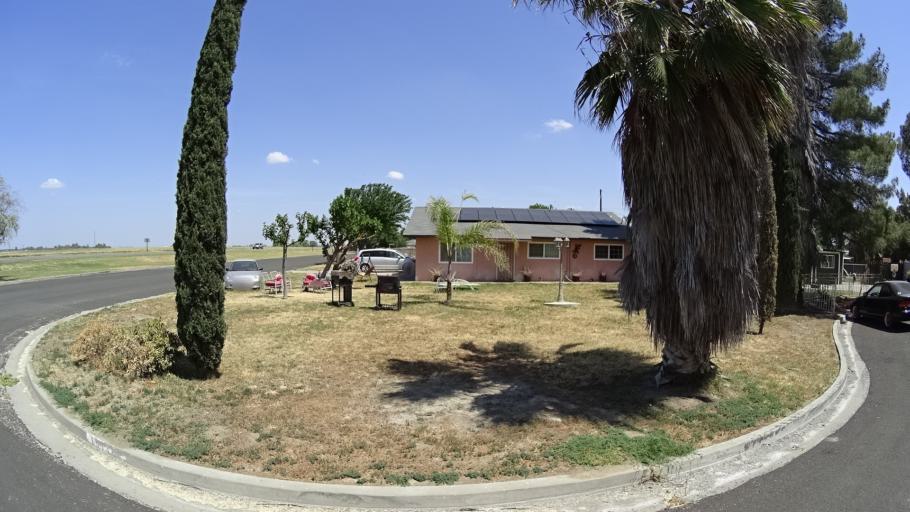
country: US
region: California
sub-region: Kings County
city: Stratford
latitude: 36.1941
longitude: -119.8240
